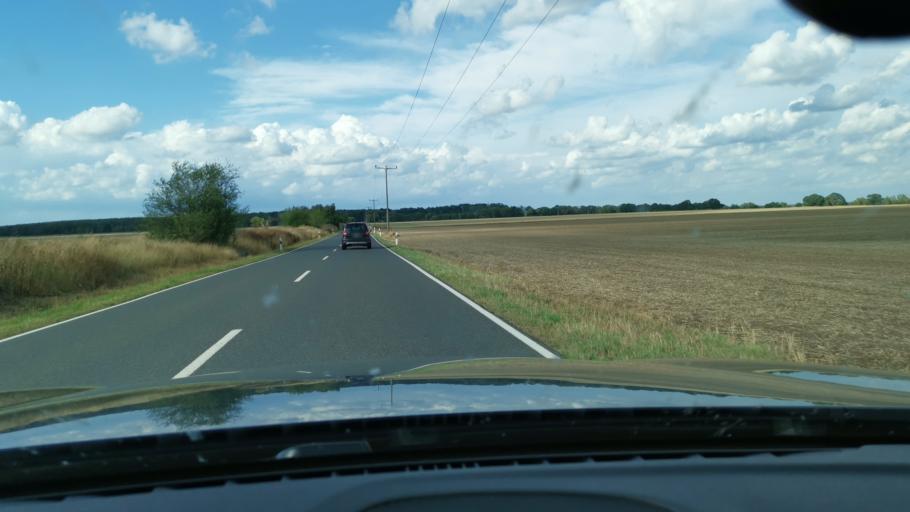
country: DE
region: Saxony
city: Zschepplin
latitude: 51.5148
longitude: 12.6003
